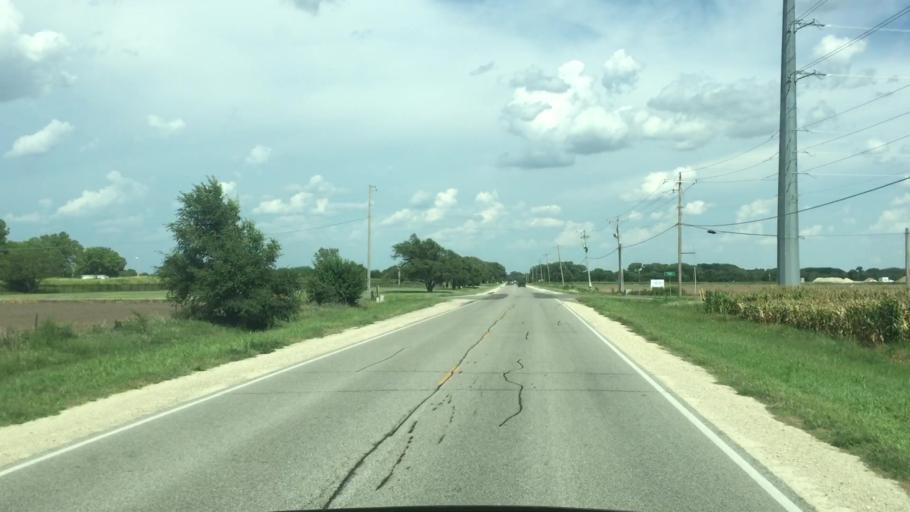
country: US
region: Kansas
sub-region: Sedgwick County
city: Maize
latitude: 37.7810
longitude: -97.4459
